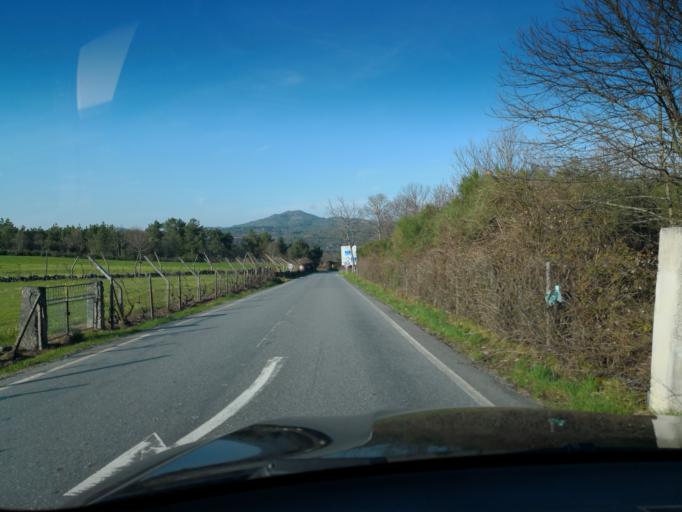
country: PT
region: Vila Real
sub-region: Sabrosa
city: Sabrosa
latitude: 41.3515
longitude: -7.6039
